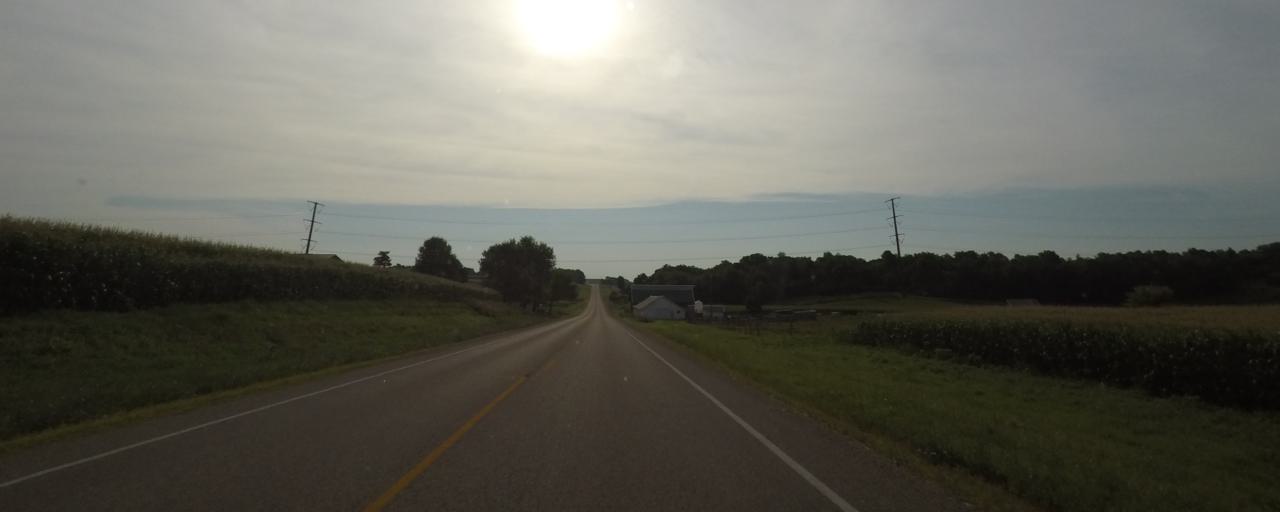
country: US
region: Wisconsin
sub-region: Columbia County
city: Lodi
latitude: 43.2357
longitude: -89.5350
